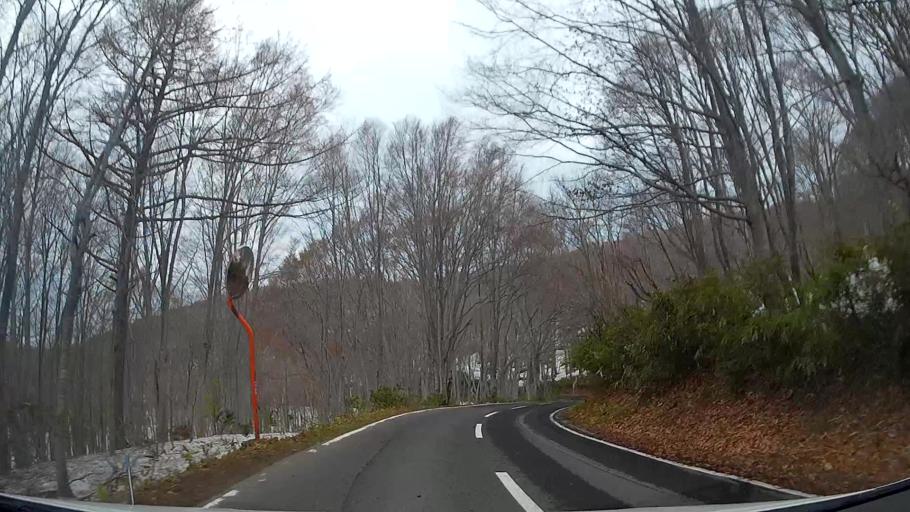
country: JP
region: Aomori
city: Aomori Shi
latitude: 40.6505
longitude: 140.8448
